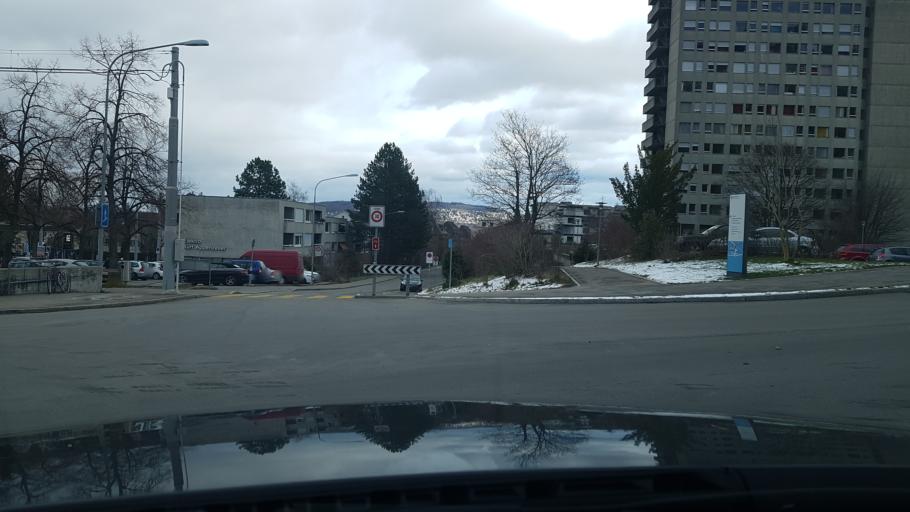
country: CH
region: Zurich
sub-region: Bezirk Zuerich
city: Zuerich (Kreis 9) / Albisrieden
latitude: 47.3675
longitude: 8.4958
